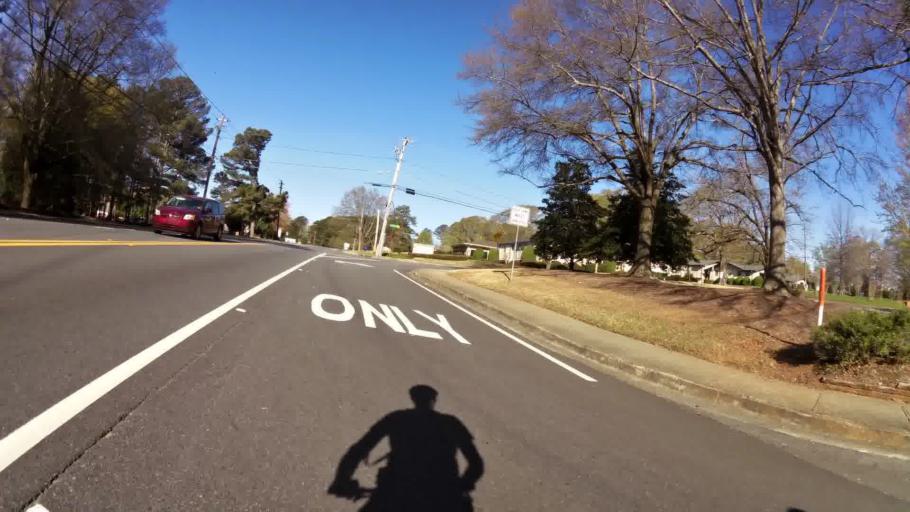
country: US
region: Georgia
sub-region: DeKalb County
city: Clarkston
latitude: 33.8410
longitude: -84.2621
